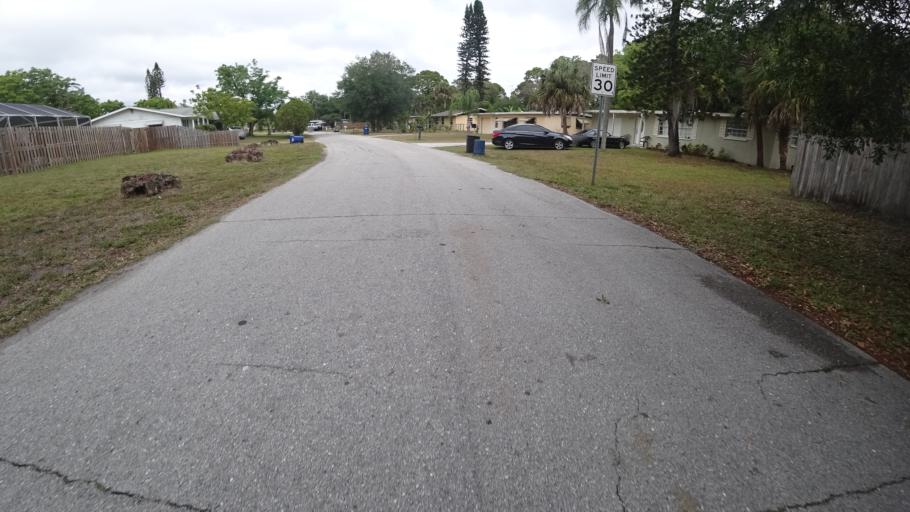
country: US
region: Florida
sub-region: Manatee County
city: South Bradenton
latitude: 27.4503
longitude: -82.5851
